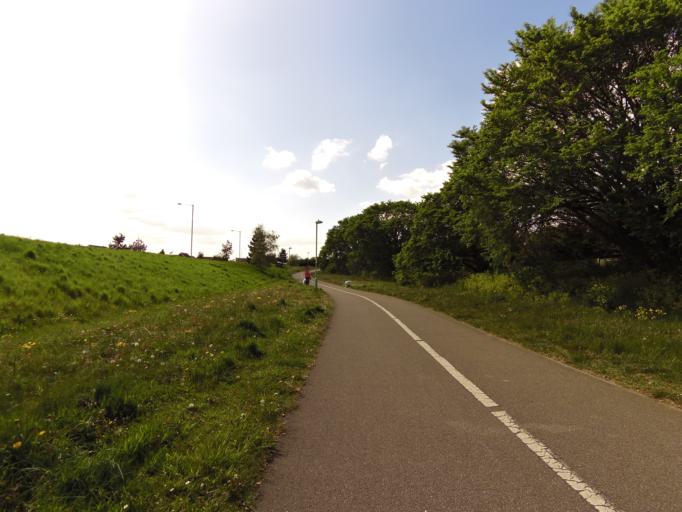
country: GB
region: England
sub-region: Suffolk
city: Kessingland
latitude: 52.4548
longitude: 1.7020
